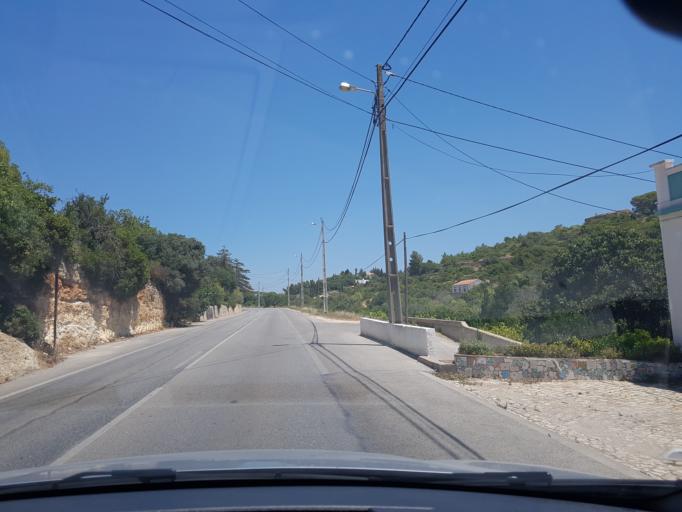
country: PT
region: Faro
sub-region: Lagoa
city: Carvoeiro
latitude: 37.1036
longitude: -8.4641
